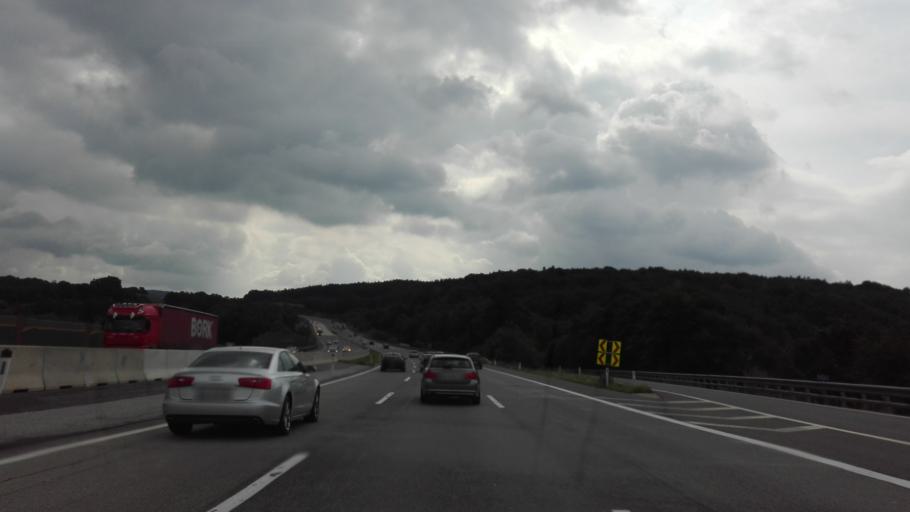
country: AT
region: Lower Austria
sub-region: Politischer Bezirk Sankt Polten
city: Kirchstetten
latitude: 48.1750
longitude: 15.8428
